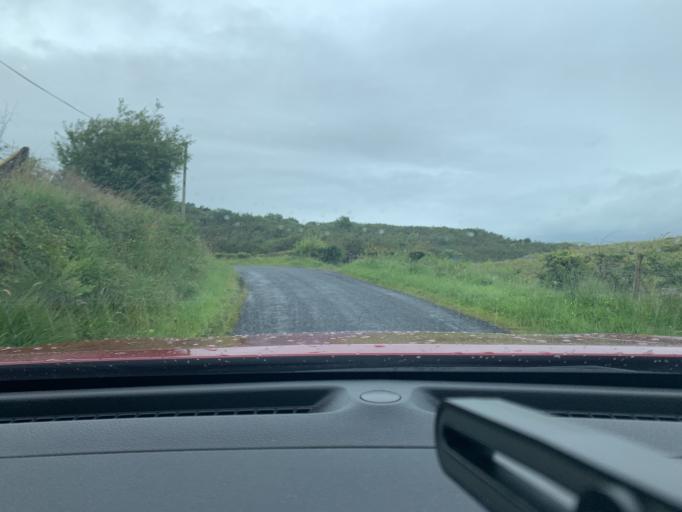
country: GB
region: Northern Ireland
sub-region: Fermanagh District
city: Enniskillen
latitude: 54.2532
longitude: -7.8275
